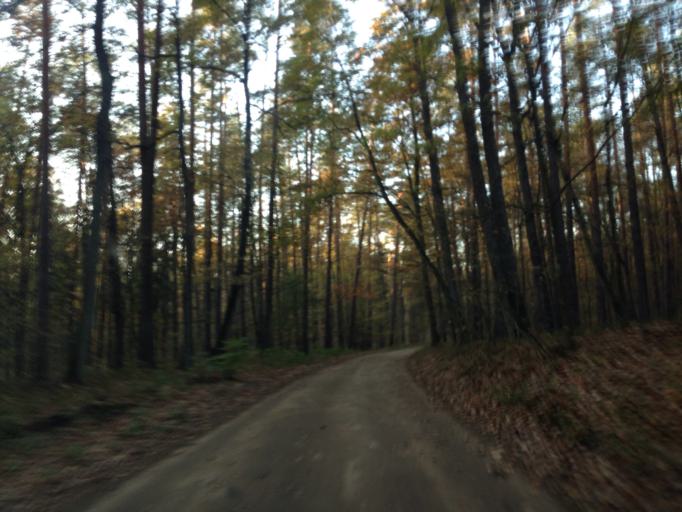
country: PL
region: Kujawsko-Pomorskie
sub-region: Powiat brodnicki
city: Gorzno
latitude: 53.1960
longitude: 19.6959
